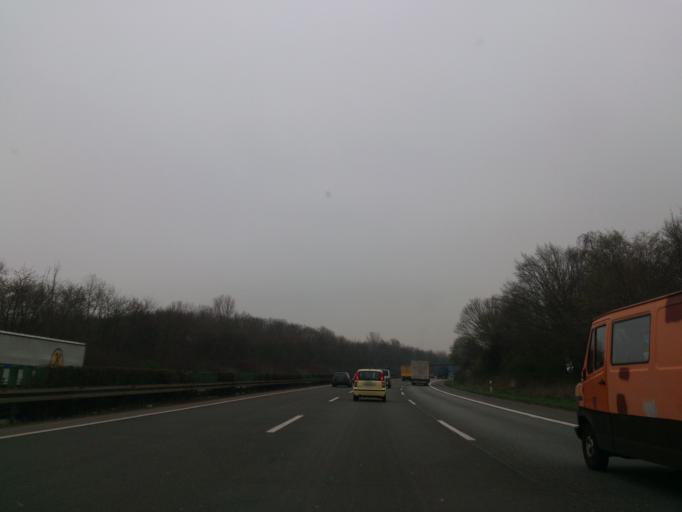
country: DE
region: North Rhine-Westphalia
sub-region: Regierungsbezirk Dusseldorf
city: Dusseldorf
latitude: 51.1700
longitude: 6.7749
